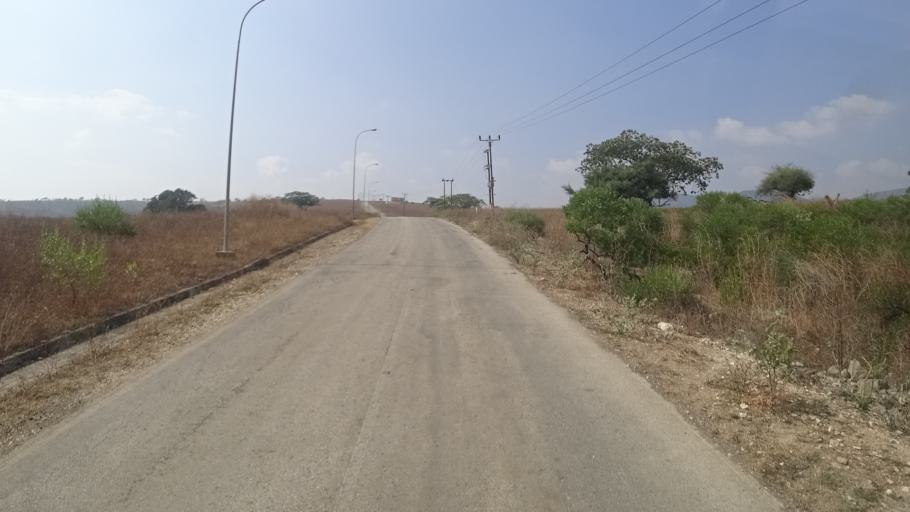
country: YE
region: Al Mahrah
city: Hawf
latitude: 16.7296
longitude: 53.2732
